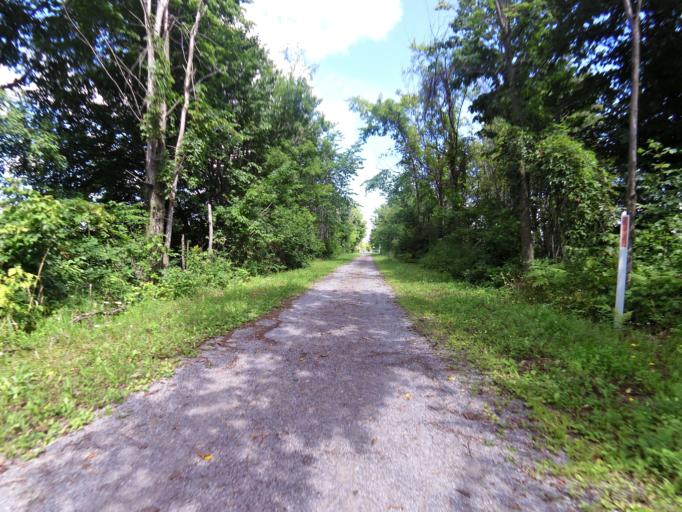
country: CA
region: Ontario
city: Ottawa
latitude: 45.2962
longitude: -75.6277
